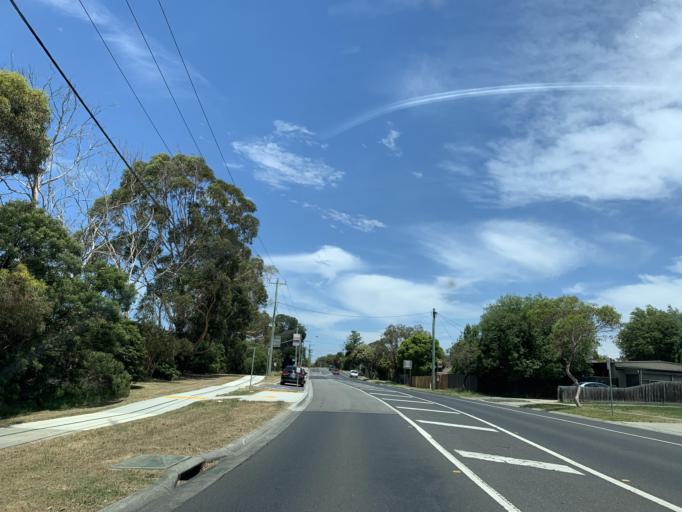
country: AU
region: Victoria
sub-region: Frankston
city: Langwarrin
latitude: -38.1615
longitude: 145.1894
